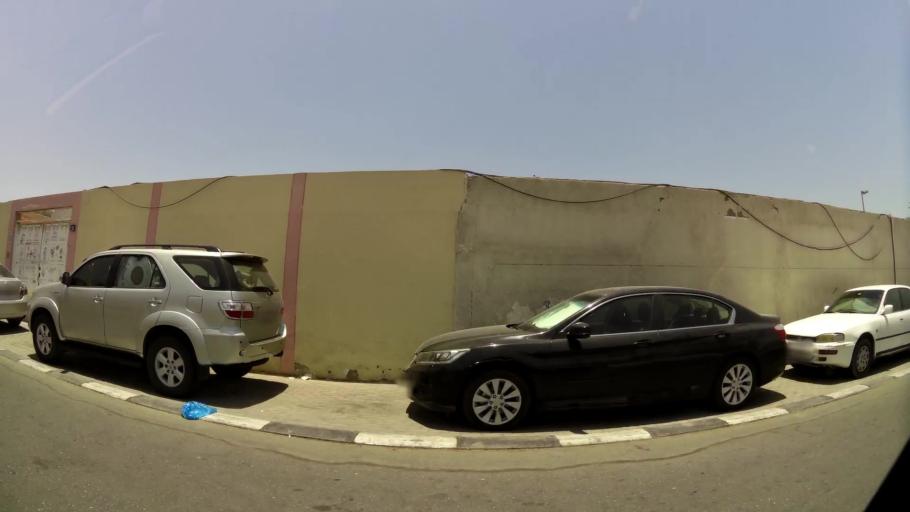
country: AE
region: Ash Shariqah
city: Sharjah
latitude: 25.2411
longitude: 55.2857
